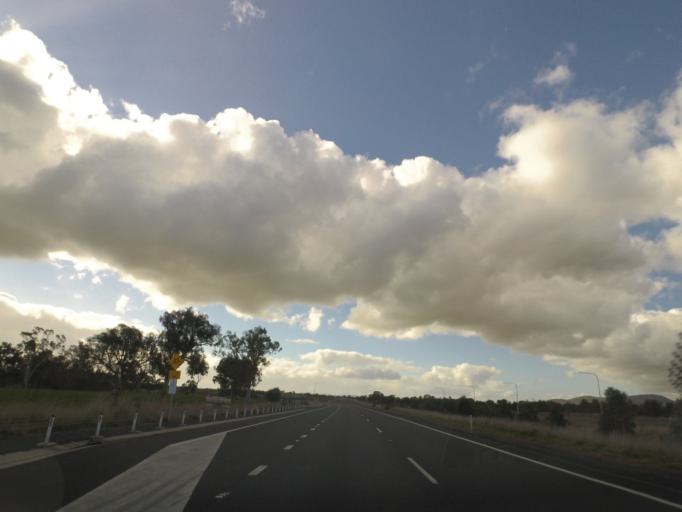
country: AU
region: New South Wales
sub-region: Greater Hume Shire
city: Holbrook
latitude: -35.7387
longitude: 147.3038
